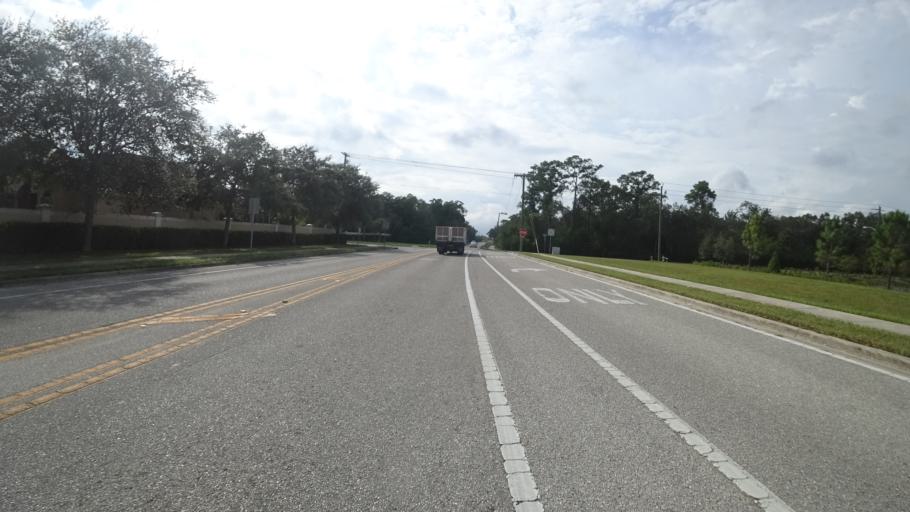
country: US
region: Florida
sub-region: Manatee County
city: Samoset
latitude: 27.4291
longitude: -82.5129
